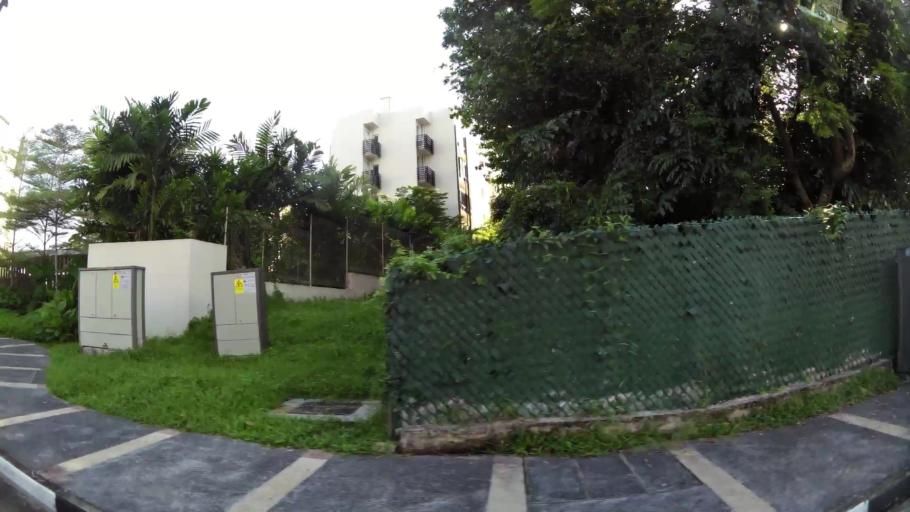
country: SG
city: Singapore
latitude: 1.3170
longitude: 103.9225
